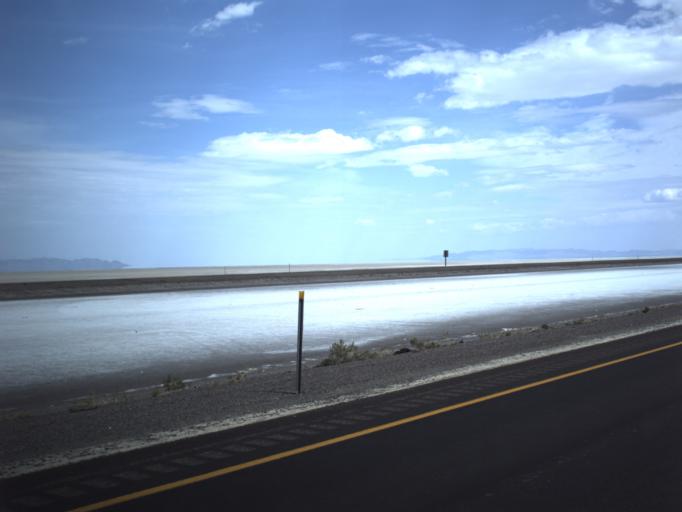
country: US
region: Utah
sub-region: Tooele County
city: Wendover
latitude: 40.7345
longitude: -113.6589
